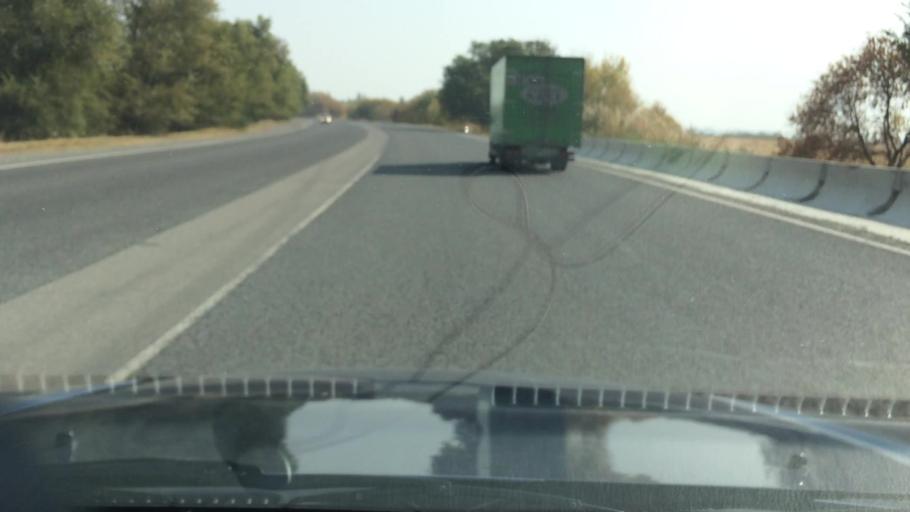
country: KG
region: Chuy
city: Ivanovka
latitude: 42.9399
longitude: 74.9711
